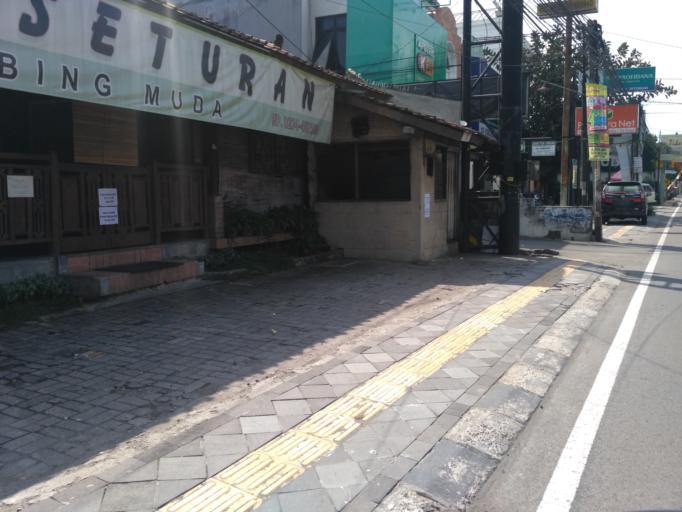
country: ID
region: Daerah Istimewa Yogyakarta
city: Depok
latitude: -7.7679
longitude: 110.4103
